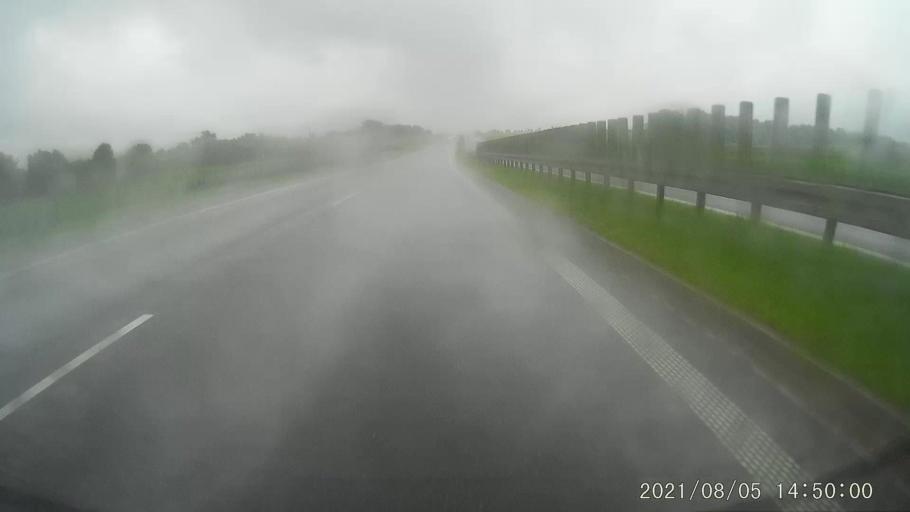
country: PL
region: Opole Voivodeship
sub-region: Powiat nyski
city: Nysa
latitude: 50.4846
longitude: 17.2696
